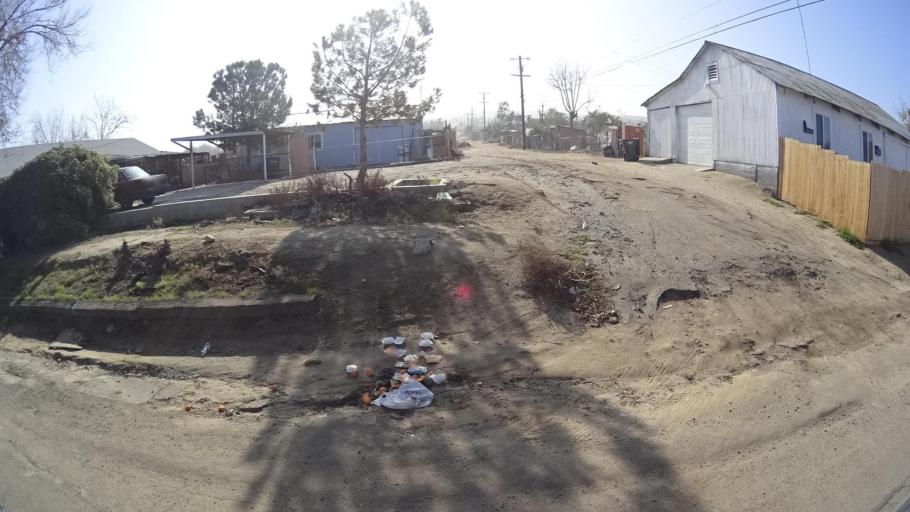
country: US
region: California
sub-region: Kern County
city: South Taft
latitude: 35.1331
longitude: -119.4605
